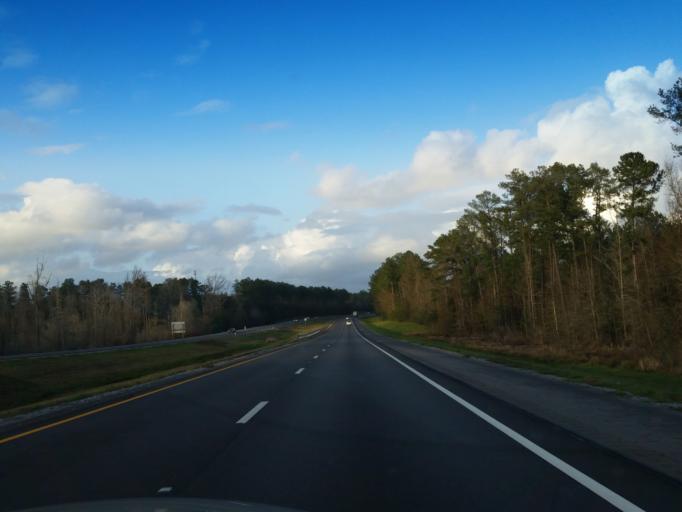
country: US
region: Mississippi
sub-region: Jones County
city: Sharon
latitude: 31.8676
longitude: -89.0460
